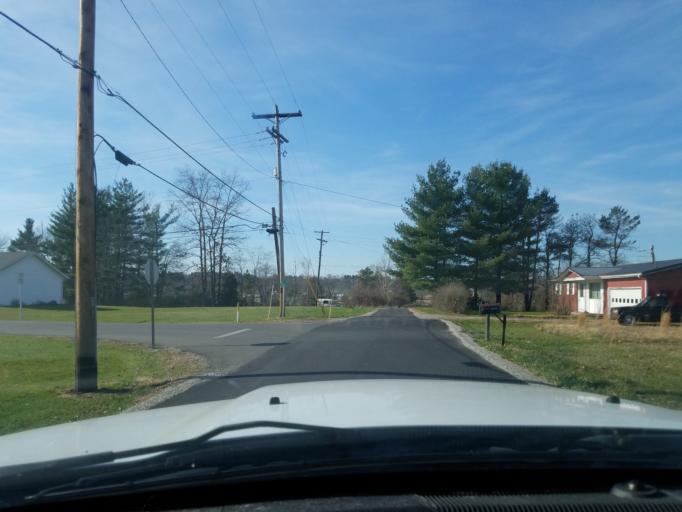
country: US
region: Ohio
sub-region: Athens County
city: Athens
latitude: 39.2326
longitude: -82.1945
